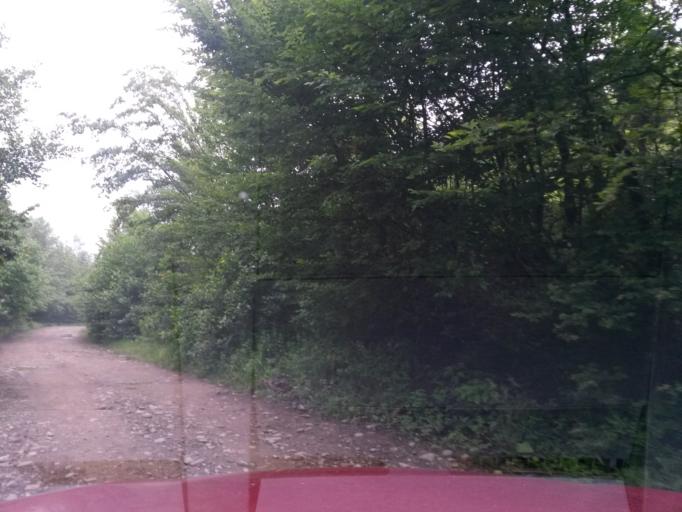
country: UA
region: Zakarpattia
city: Velykyi Bereznyi
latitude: 48.9077
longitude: 22.4716
